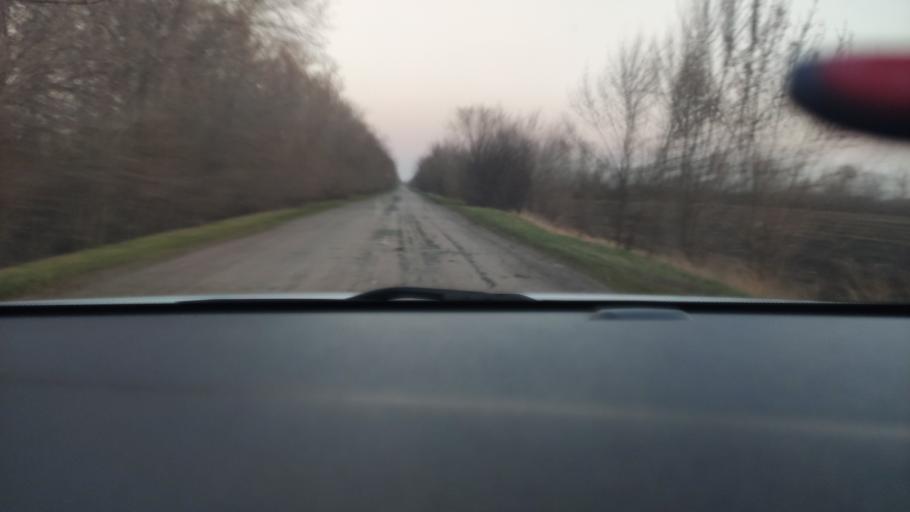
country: RU
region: Voronezj
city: Uryv-Pokrovka
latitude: 51.1344
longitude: 39.0914
